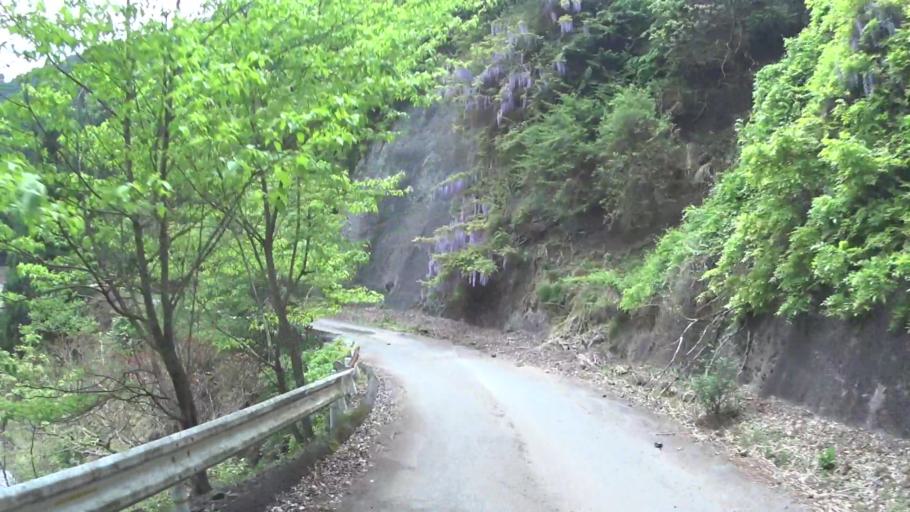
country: JP
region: Kyoto
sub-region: Kyoto-shi
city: Kamigyo-ku
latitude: 35.1929
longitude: 135.7019
